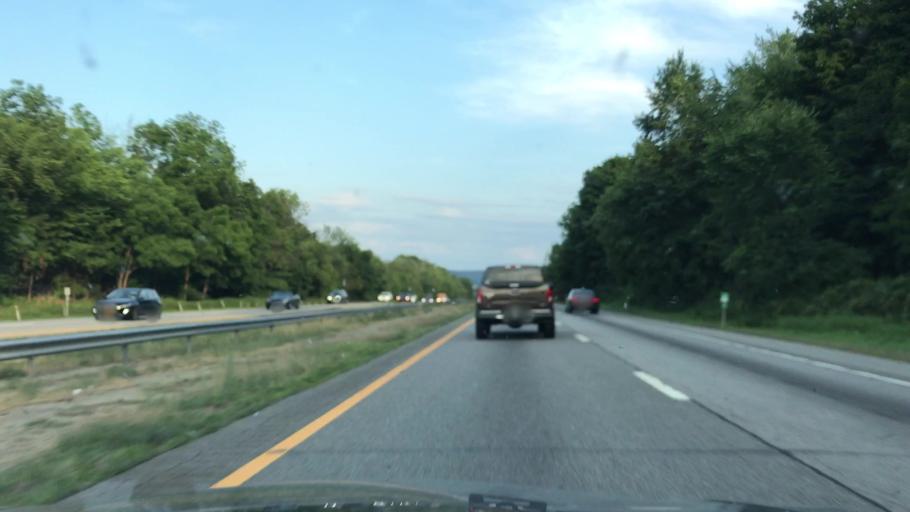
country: US
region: New York
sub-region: Orange County
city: Kiryas Joel
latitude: 41.3369
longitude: -74.1755
